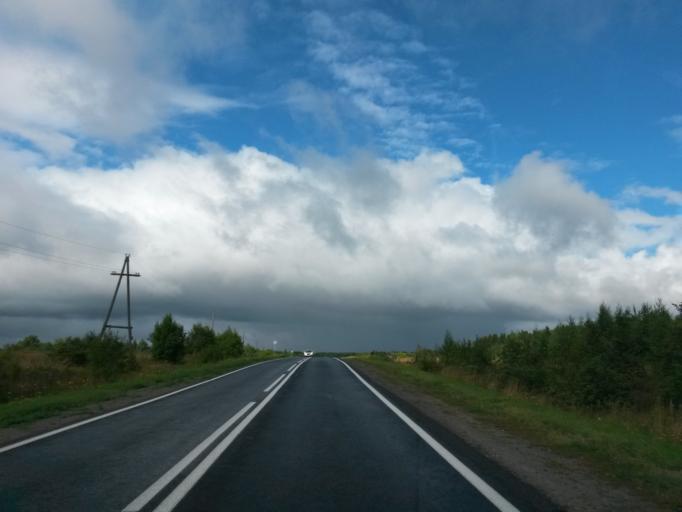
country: RU
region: Jaroslavl
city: Konstantinovskiy
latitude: 57.8180
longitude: 39.7072
